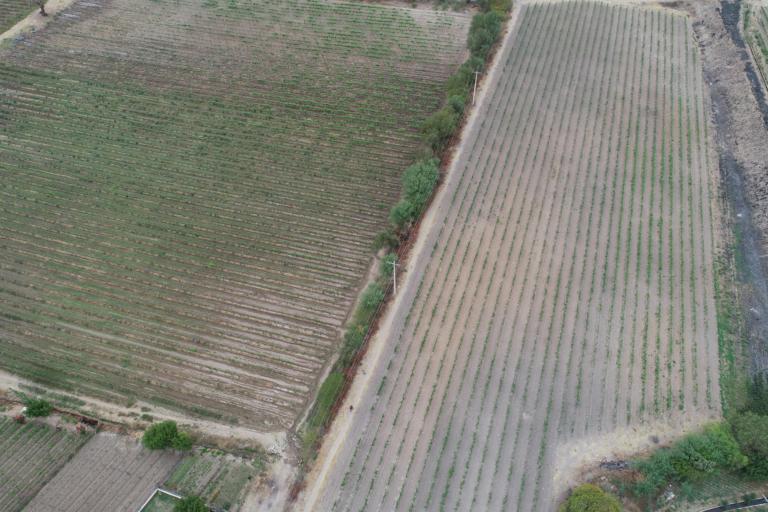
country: BO
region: Tarija
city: Tarija
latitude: -21.5951
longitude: -64.6251
